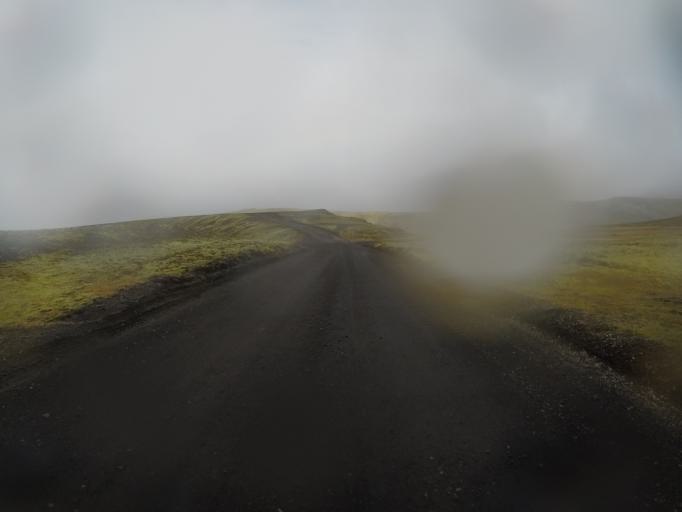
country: IS
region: South
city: Vestmannaeyjar
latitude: 63.9771
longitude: -18.8439
